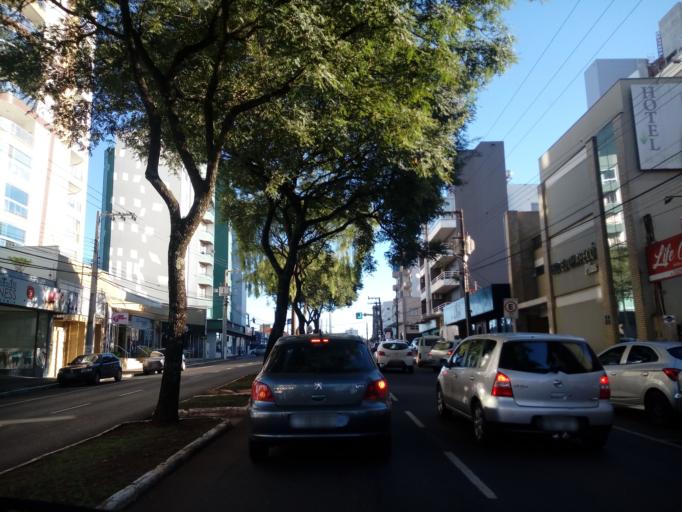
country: BR
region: Santa Catarina
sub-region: Chapeco
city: Chapeco
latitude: -27.0925
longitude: -52.6156
